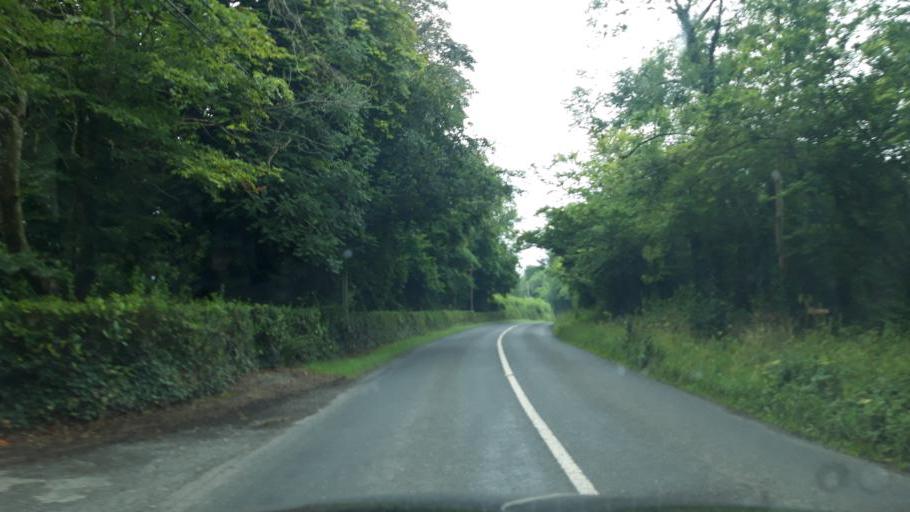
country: IE
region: Munster
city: Fethard
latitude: 52.5380
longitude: -7.6811
